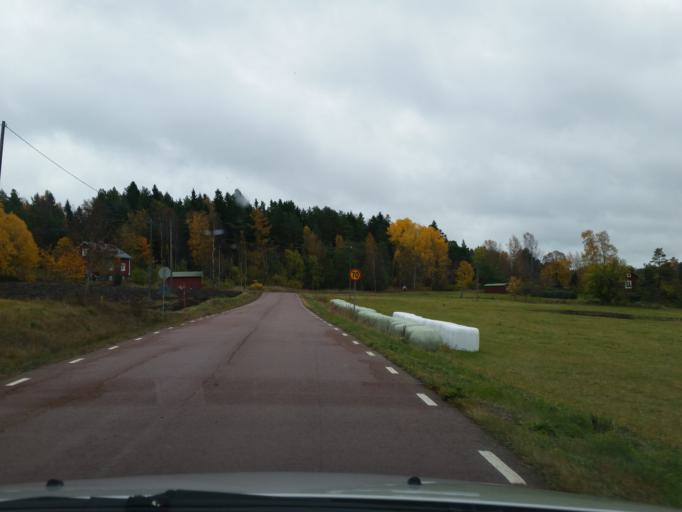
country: AX
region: Alands landsbygd
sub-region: Lumparland
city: Lumparland
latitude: 60.1375
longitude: 20.2717
